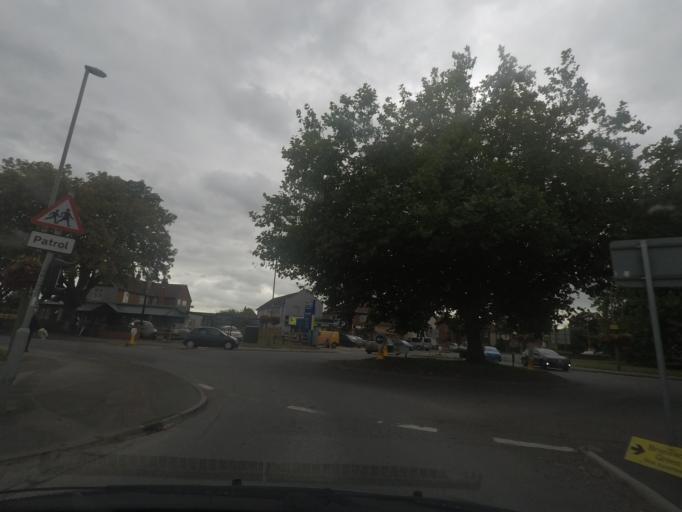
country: GB
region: England
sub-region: Oxfordshire
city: Didcot
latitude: 51.6061
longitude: -1.2515
